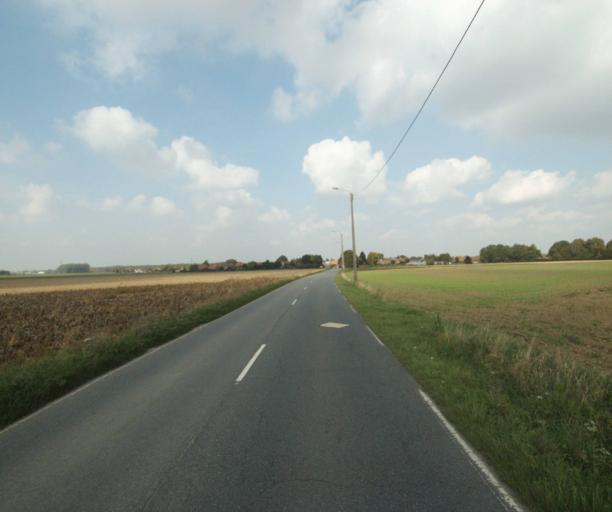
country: FR
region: Nord-Pas-de-Calais
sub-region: Departement du Nord
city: Houplin-Ancoisne
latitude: 50.5711
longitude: 3.0201
